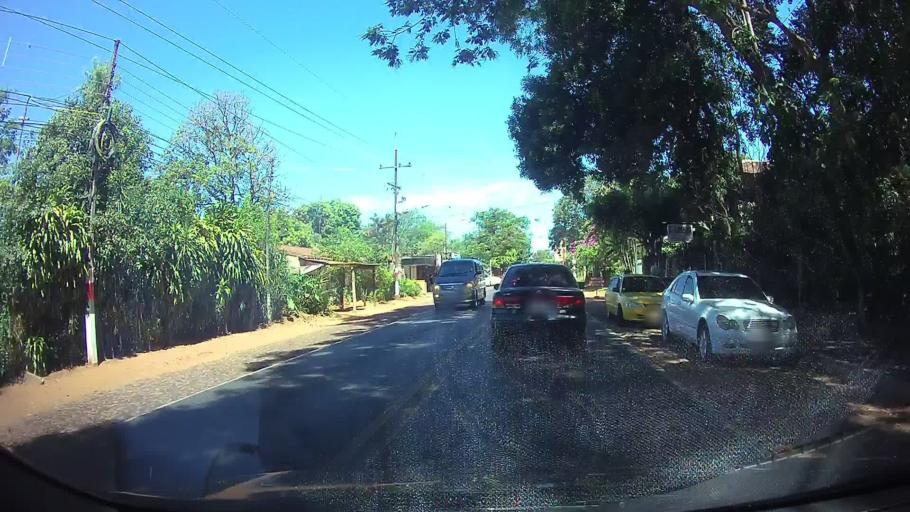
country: PY
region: Central
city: Aregua
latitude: -25.2993
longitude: -57.4102
